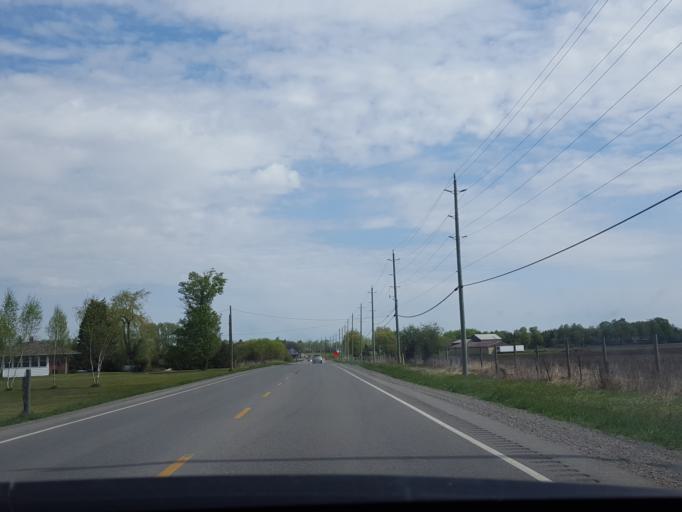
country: CA
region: Ontario
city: Uxbridge
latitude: 44.1652
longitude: -78.8961
